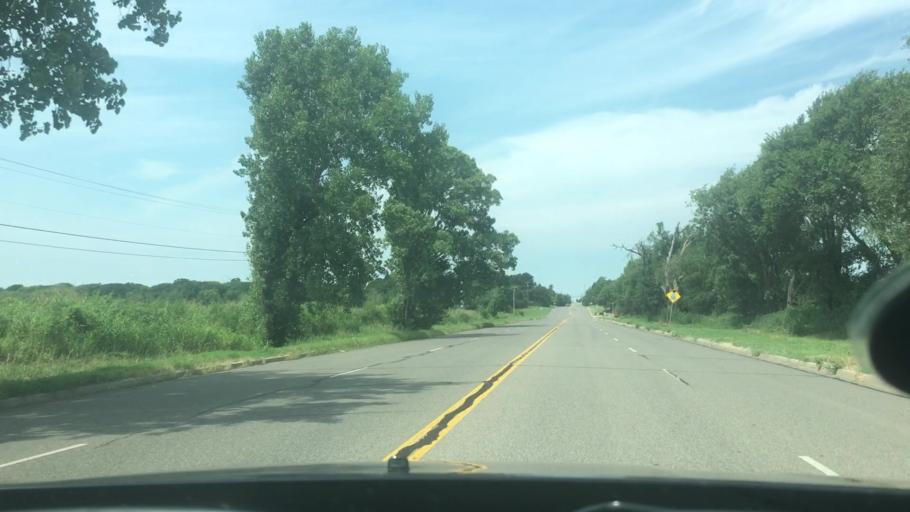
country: US
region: Oklahoma
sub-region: Pottawatomie County
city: Shawnee
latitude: 35.3326
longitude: -96.8830
